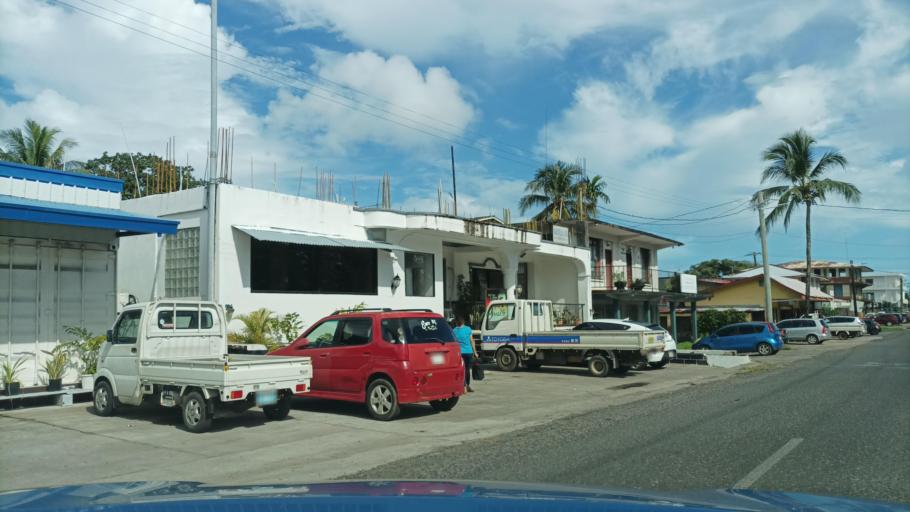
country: FM
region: Pohnpei
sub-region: Kolonia Municipality
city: Kolonia
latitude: 6.9647
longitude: 158.2112
